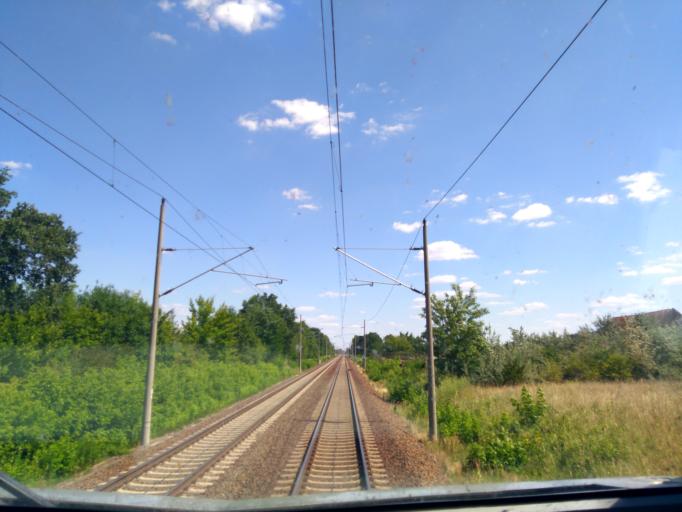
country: DE
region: Brandenburg
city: Kyritz
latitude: 52.8907
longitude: 12.3528
